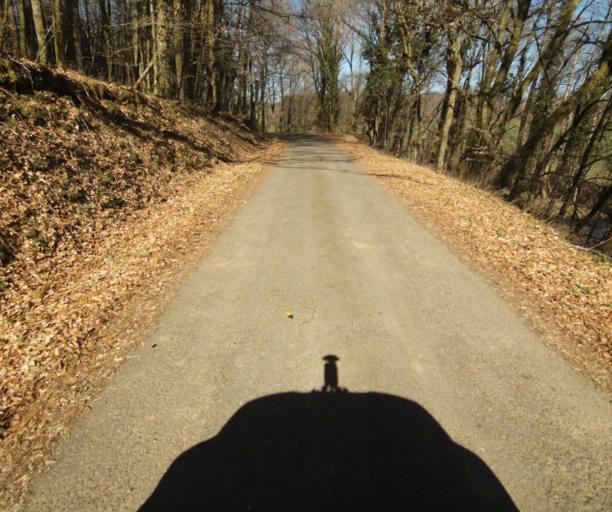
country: FR
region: Limousin
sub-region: Departement de la Correze
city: Chamboulive
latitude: 45.4175
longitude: 1.7194
